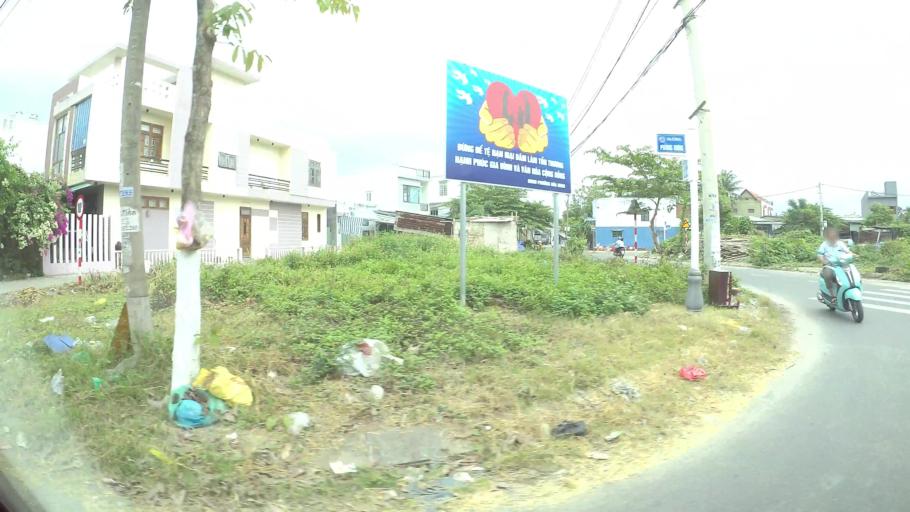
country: VN
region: Da Nang
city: Lien Chieu
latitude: 16.0722
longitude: 108.1660
